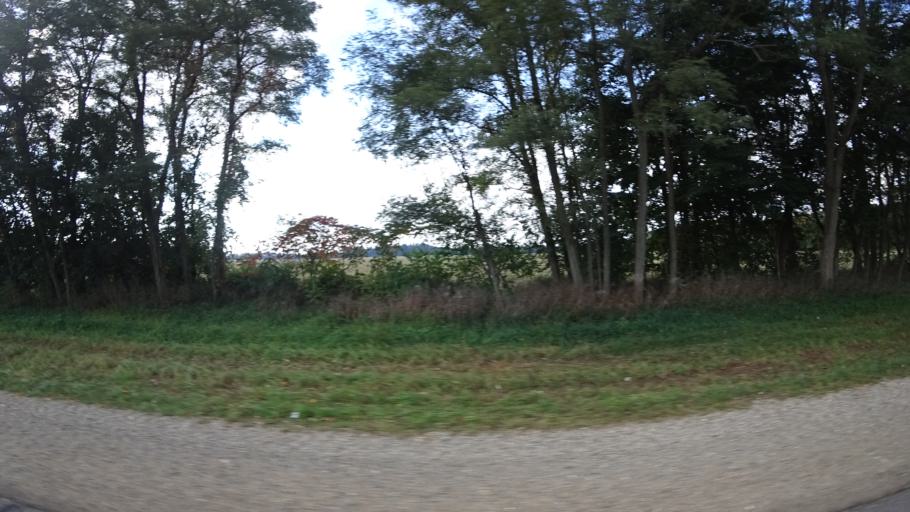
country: US
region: Michigan
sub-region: Saint Joseph County
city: Centreville
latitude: 41.9751
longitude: -85.5670
